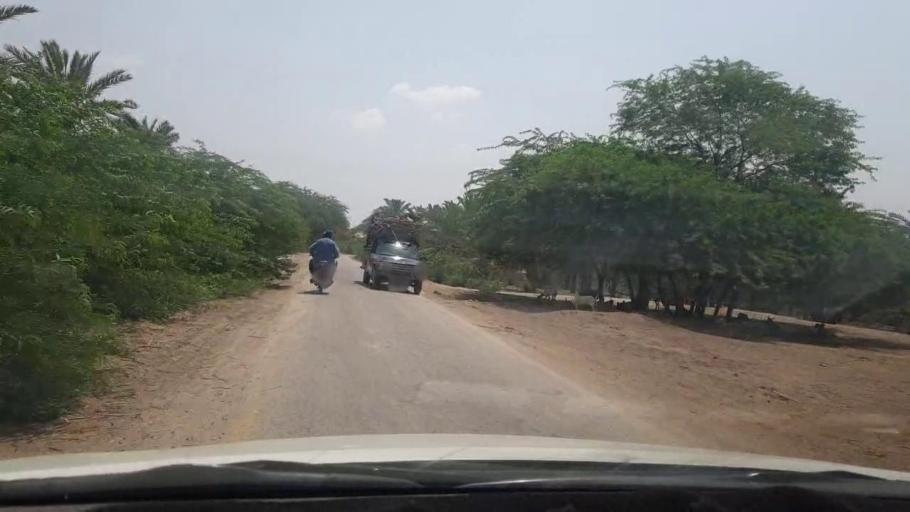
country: PK
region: Sindh
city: Khairpur
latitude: 27.5324
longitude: 68.8965
